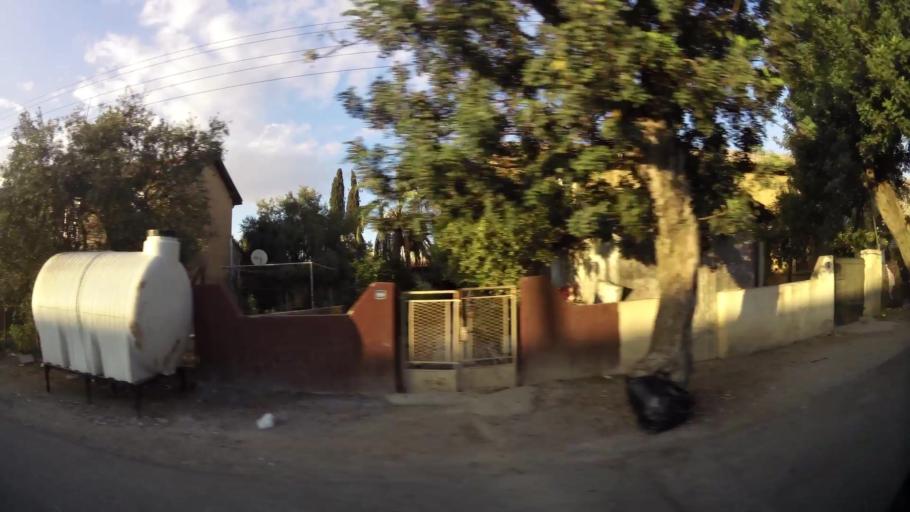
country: CY
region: Lefkosia
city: Nicosia
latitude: 35.1870
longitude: 33.3663
